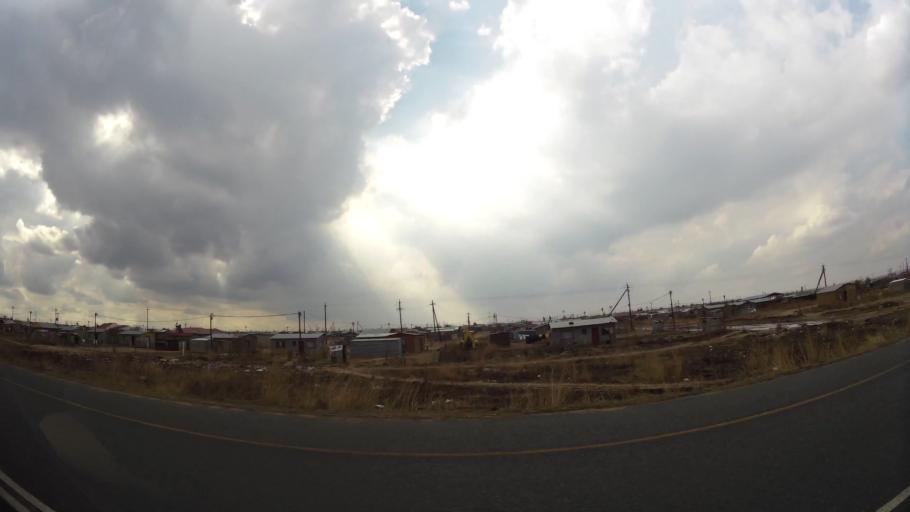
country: ZA
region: Orange Free State
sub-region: Fezile Dabi District Municipality
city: Sasolburg
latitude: -26.8662
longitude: 27.8940
